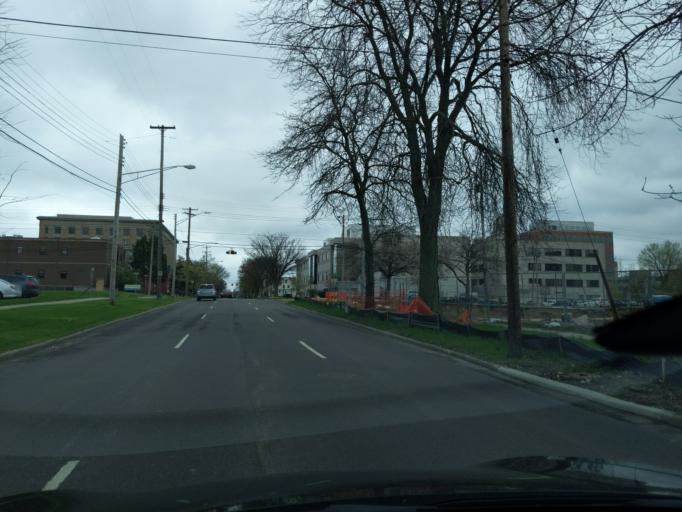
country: US
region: Michigan
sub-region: Ingham County
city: Lansing
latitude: 42.7281
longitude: -84.5571
